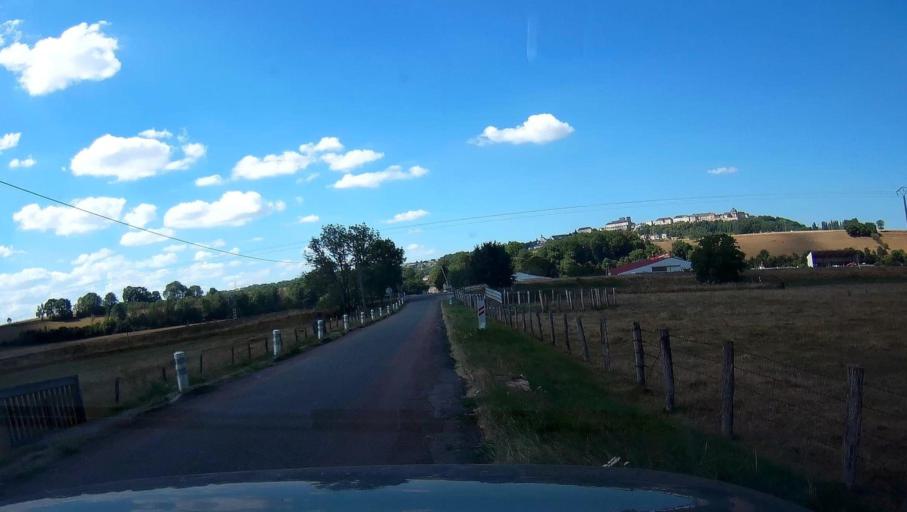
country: FR
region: Champagne-Ardenne
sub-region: Departement de la Haute-Marne
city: Langres
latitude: 47.8713
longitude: 5.3567
